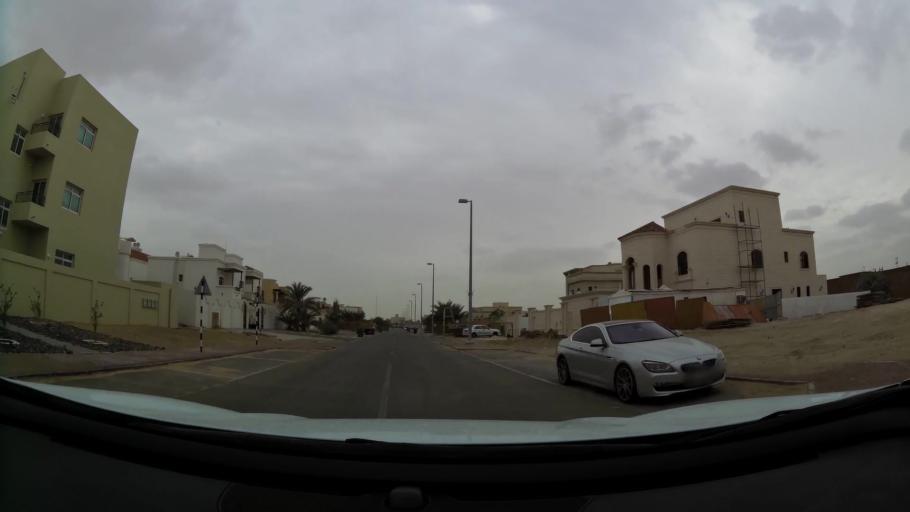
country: AE
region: Abu Dhabi
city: Abu Dhabi
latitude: 24.3763
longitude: 54.6472
